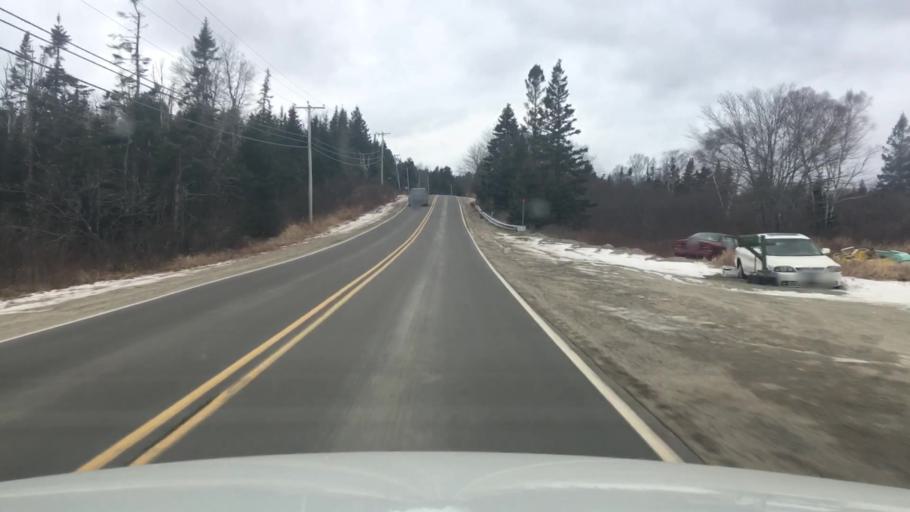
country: US
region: Maine
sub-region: Washington County
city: Jonesport
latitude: 44.5589
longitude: -67.6296
